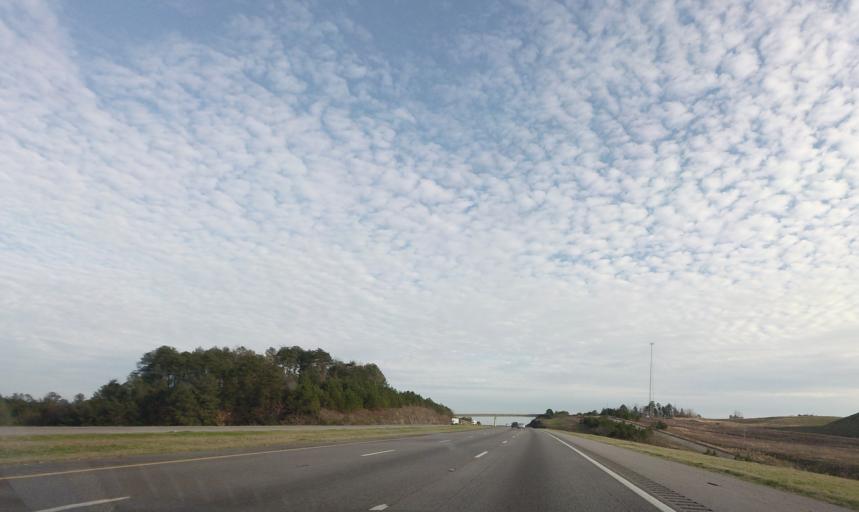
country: US
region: Alabama
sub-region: Walker County
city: Dora
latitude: 33.6950
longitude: -87.1268
